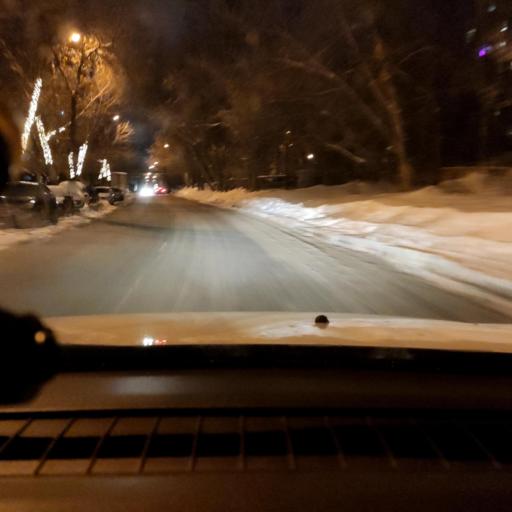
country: RU
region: Samara
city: Volzhskiy
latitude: 53.3931
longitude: 50.1706
